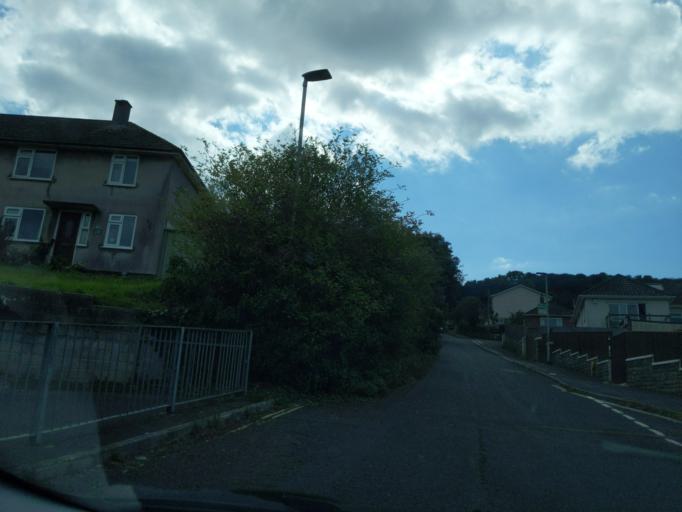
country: GB
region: England
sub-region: Plymouth
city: Plymstock
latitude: 50.3519
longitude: -4.1096
